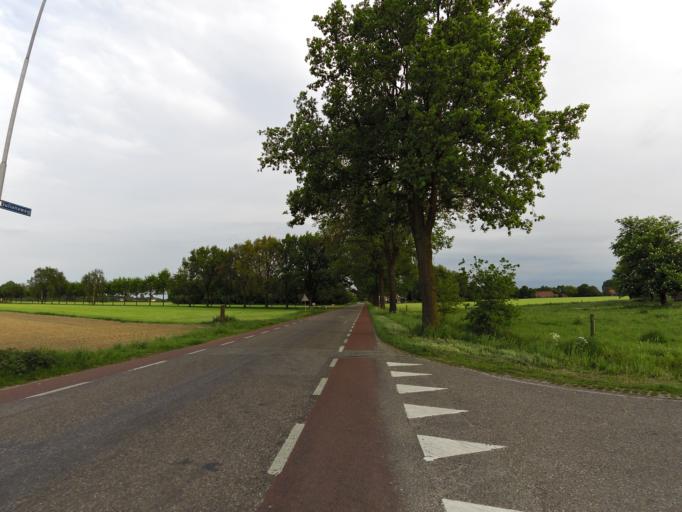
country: NL
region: Gelderland
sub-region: Oude IJsselstreek
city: Gendringen
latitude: 51.8500
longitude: 6.3875
